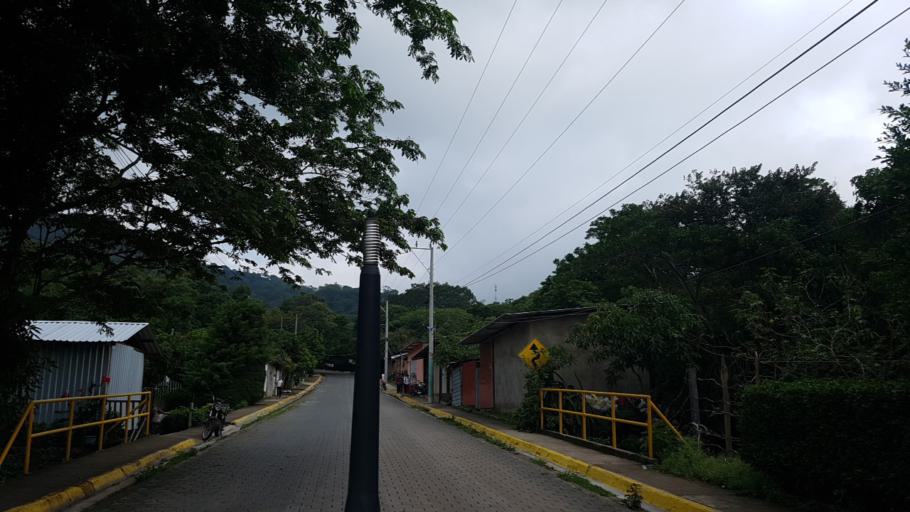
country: NI
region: Leon
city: Santa Rosa del Penon
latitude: 12.9317
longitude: -86.3463
